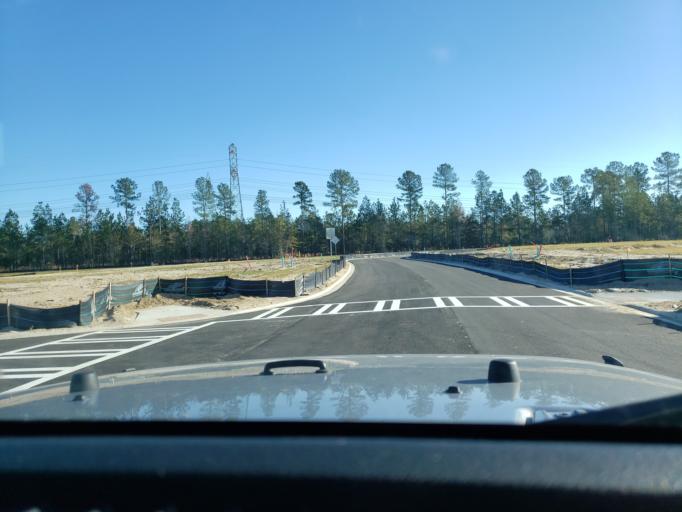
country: US
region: Georgia
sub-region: Chatham County
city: Bloomingdale
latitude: 32.0693
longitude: -81.3385
